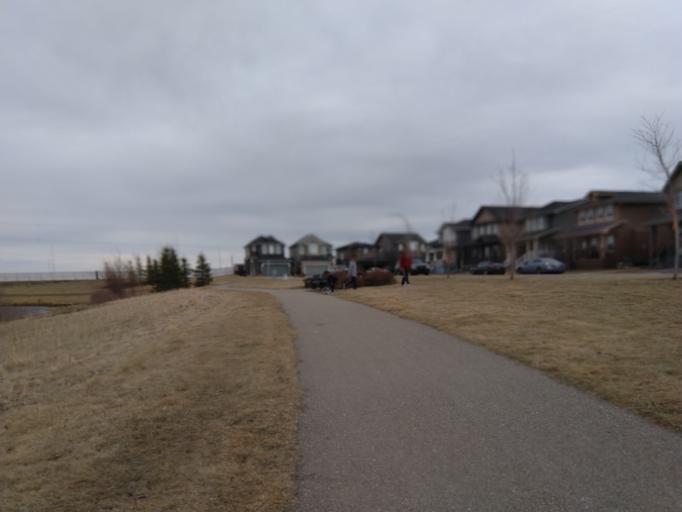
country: CA
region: Alberta
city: Calgary
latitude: 51.1731
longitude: -114.1046
